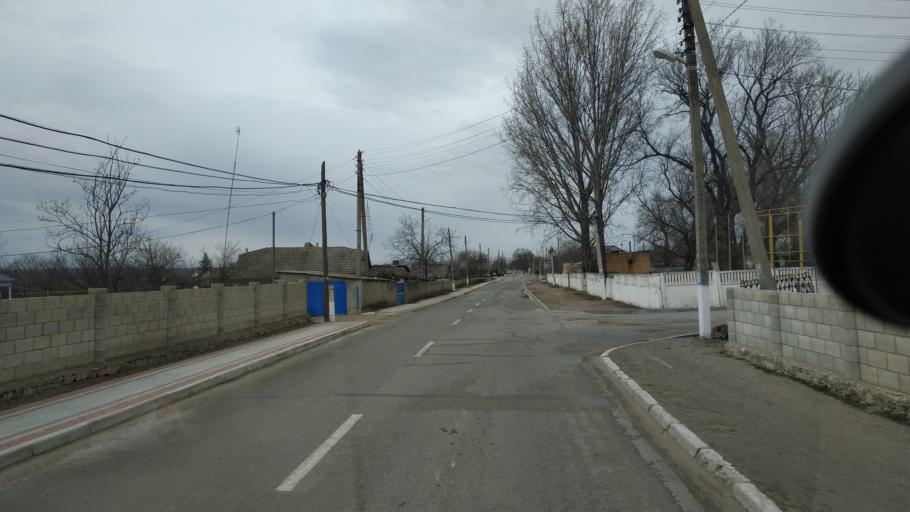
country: MD
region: Telenesti
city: Cocieri
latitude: 47.3117
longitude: 29.1066
